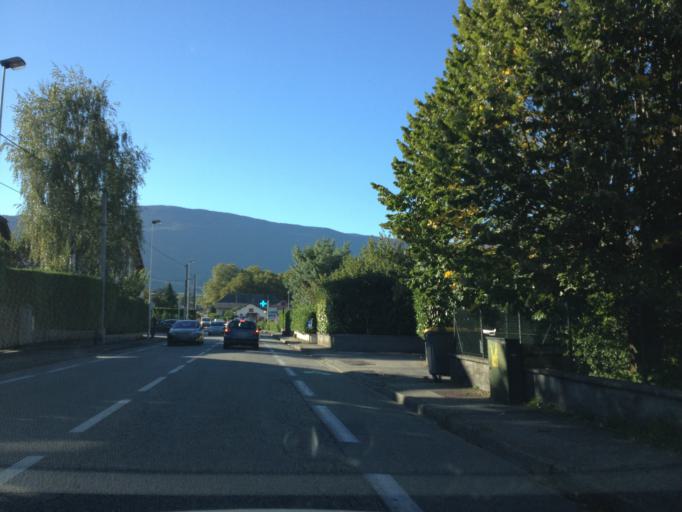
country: FR
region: Rhone-Alpes
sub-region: Departement de la Savoie
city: Cognin
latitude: 45.5797
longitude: 5.8928
